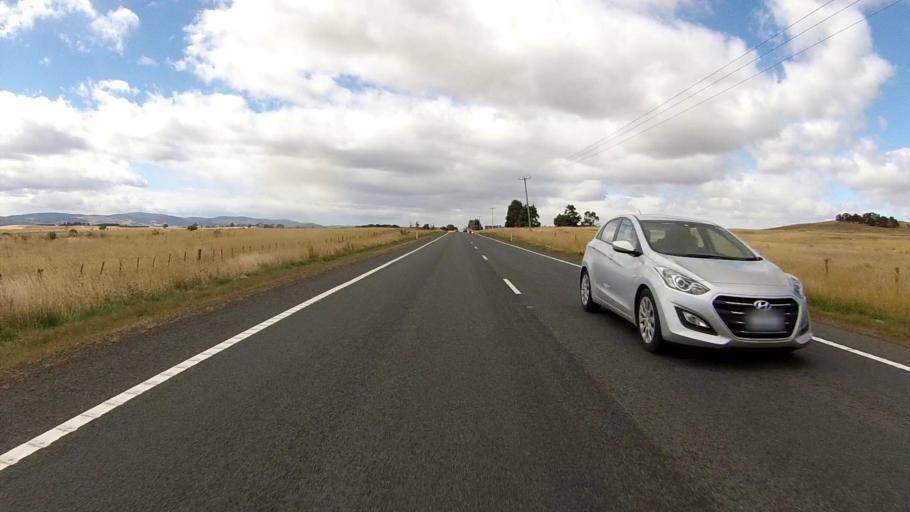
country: AU
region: Tasmania
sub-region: Northern Midlands
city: Evandale
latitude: -41.8952
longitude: 147.4730
